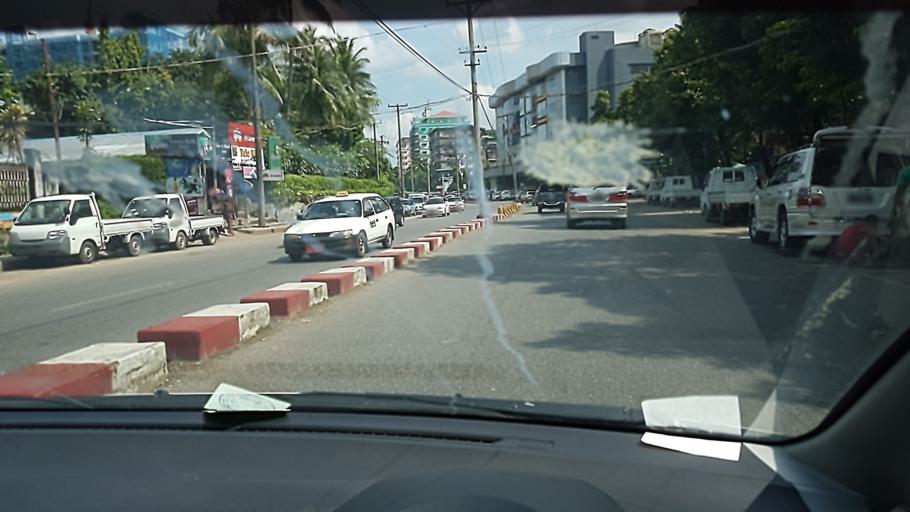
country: MM
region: Yangon
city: Yangon
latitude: 16.7968
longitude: 96.1725
